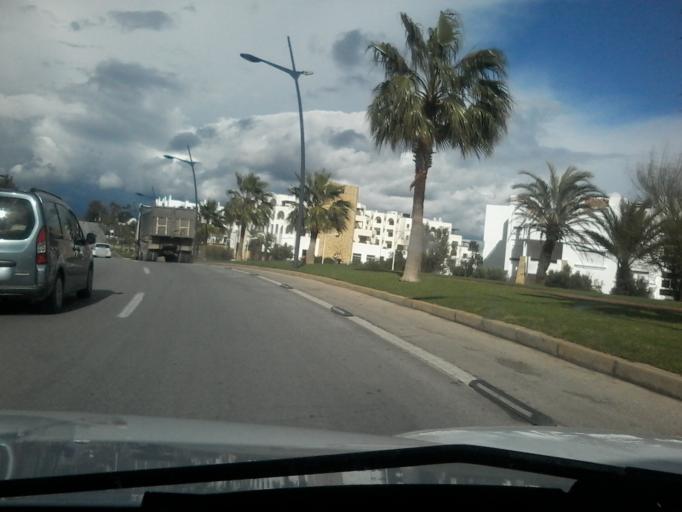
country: ES
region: Ceuta
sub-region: Ceuta
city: Ceuta
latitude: 35.7569
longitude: -5.3478
